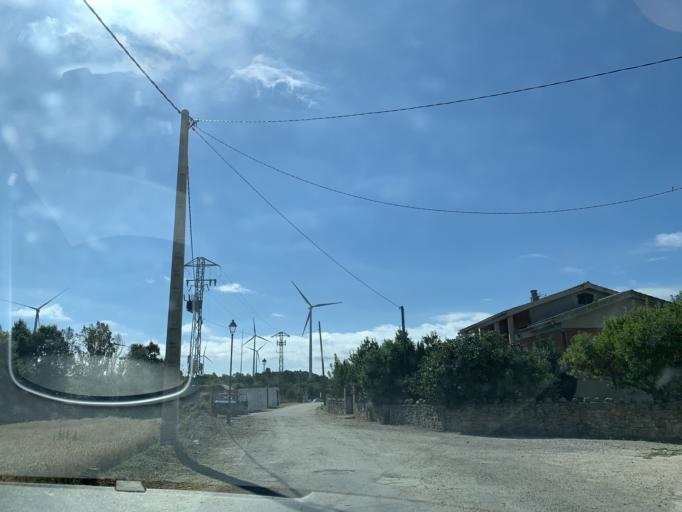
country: ES
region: Catalonia
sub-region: Provincia de Tarragona
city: Vallfogona de Riucorb
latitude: 41.5437
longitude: 1.2679
